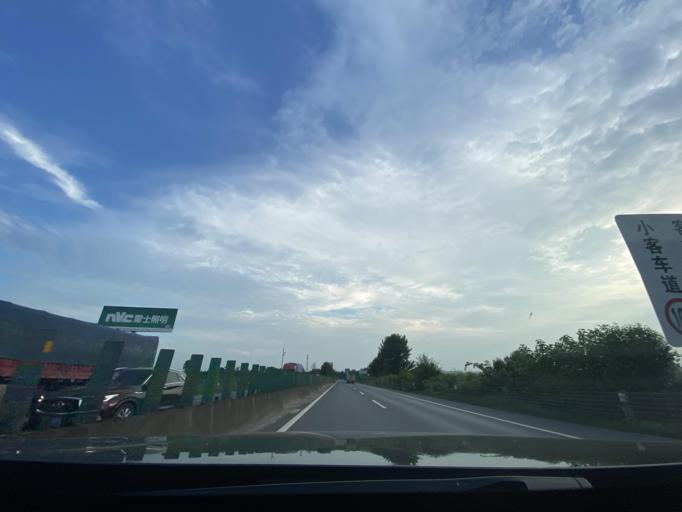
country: CN
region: Sichuan
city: Luojiang
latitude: 31.3747
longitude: 104.5463
